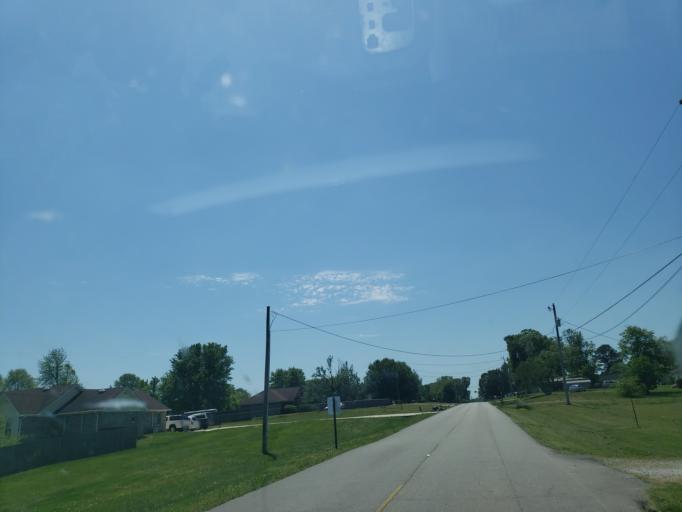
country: US
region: Alabama
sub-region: Madison County
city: Harvest
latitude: 34.9356
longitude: -86.7287
